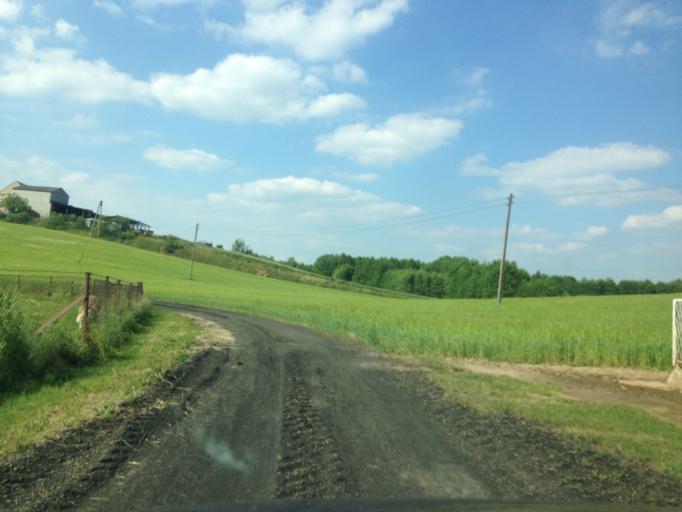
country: PL
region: Kujawsko-Pomorskie
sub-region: Powiat brodnicki
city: Bartniczka
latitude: 53.2490
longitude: 19.6335
